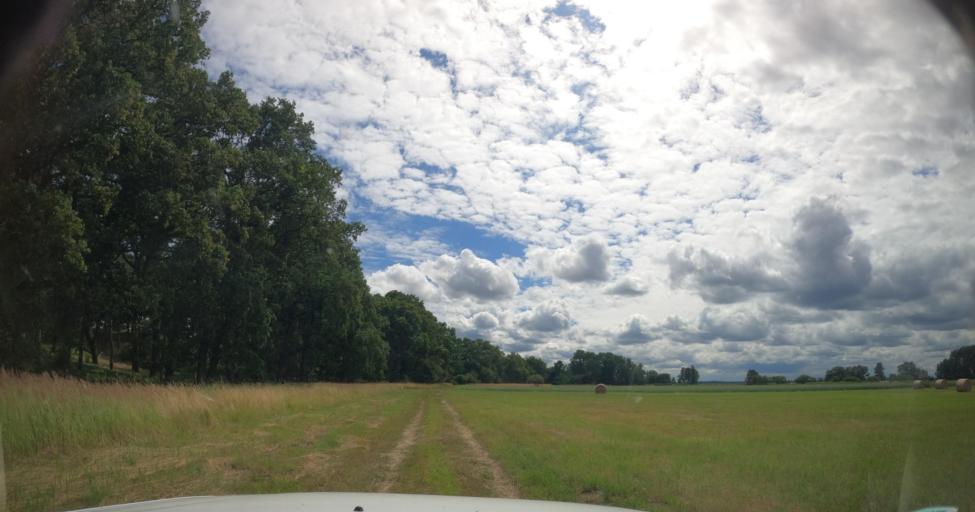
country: PL
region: West Pomeranian Voivodeship
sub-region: Powiat goleniowski
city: Stepnica
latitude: 53.7024
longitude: 14.5470
